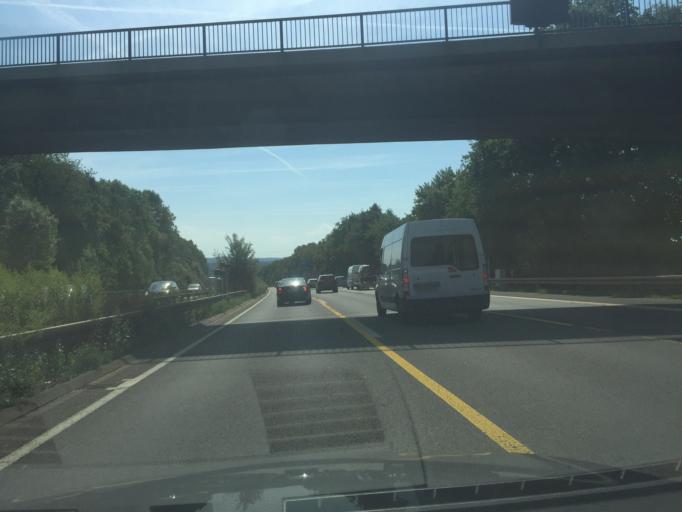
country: DE
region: North Rhine-Westphalia
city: Schwerte
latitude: 51.3947
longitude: 7.5280
